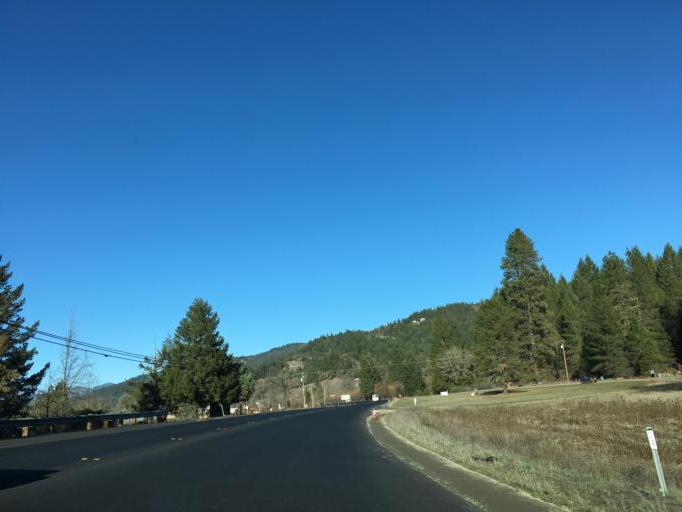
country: US
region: California
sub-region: Mendocino County
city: Laytonville
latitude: 39.6600
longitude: -123.4775
